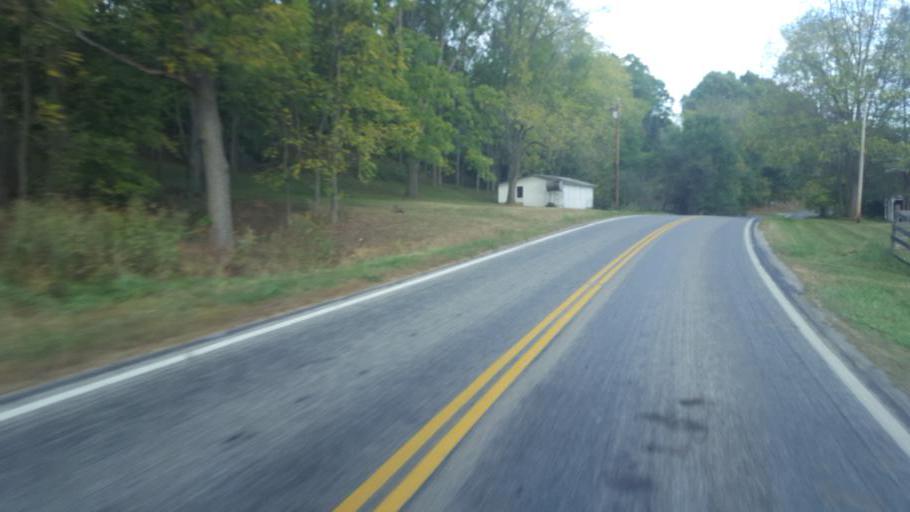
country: US
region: Ohio
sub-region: Ashland County
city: Loudonville
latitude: 40.7163
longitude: -82.1763
